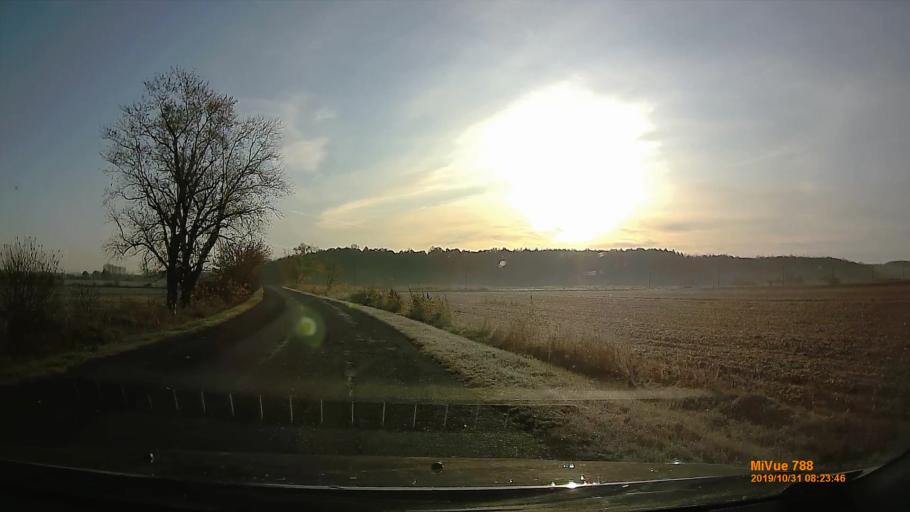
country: HU
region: Pest
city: Pand
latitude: 47.3680
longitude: 19.6498
